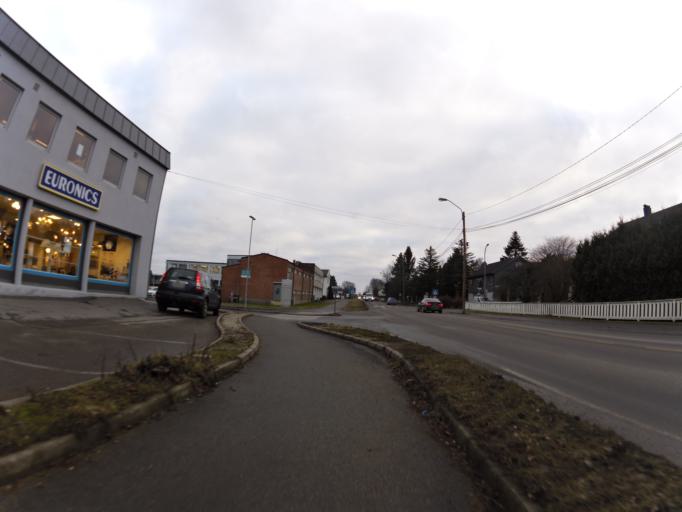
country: NO
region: Ostfold
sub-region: Fredrikstad
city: Fredrikstad
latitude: 59.2289
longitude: 10.9102
